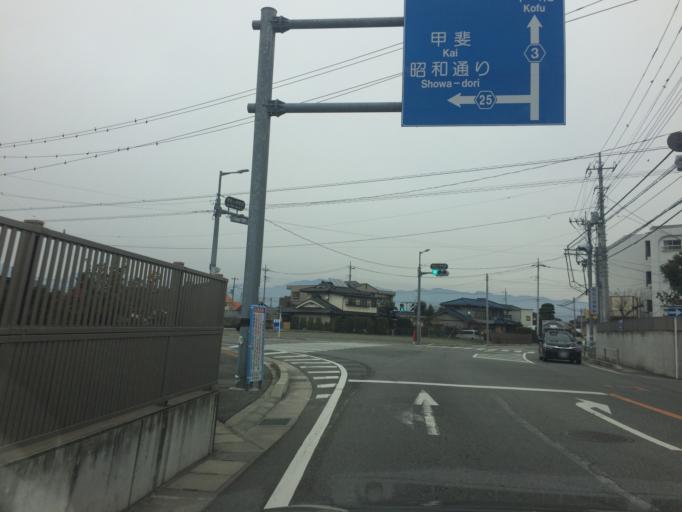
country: JP
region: Yamanashi
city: Ryuo
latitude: 35.6156
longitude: 138.5276
